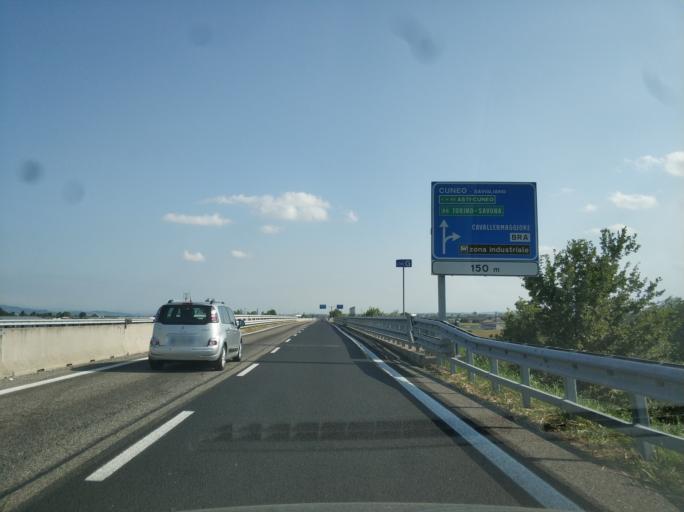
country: IT
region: Piedmont
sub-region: Provincia di Cuneo
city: Bra
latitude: 44.6953
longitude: 7.8252
